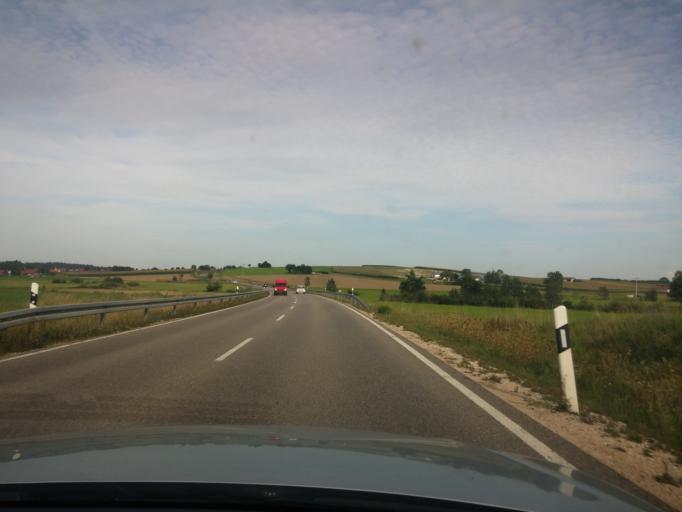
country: DE
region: Baden-Wuerttemberg
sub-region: Tuebingen Region
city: Uttenweiler
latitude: 48.1422
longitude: 9.5956
